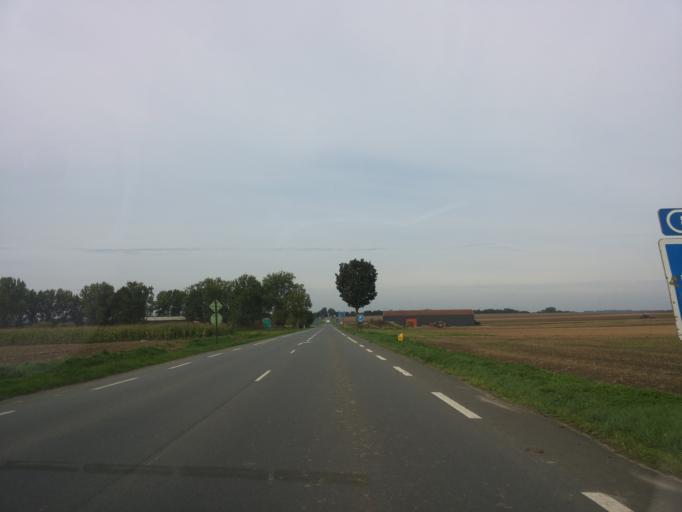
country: FR
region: Nord-Pas-de-Calais
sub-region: Departement du Pas-de-Calais
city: Bourlon
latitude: 50.2041
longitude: 3.1136
